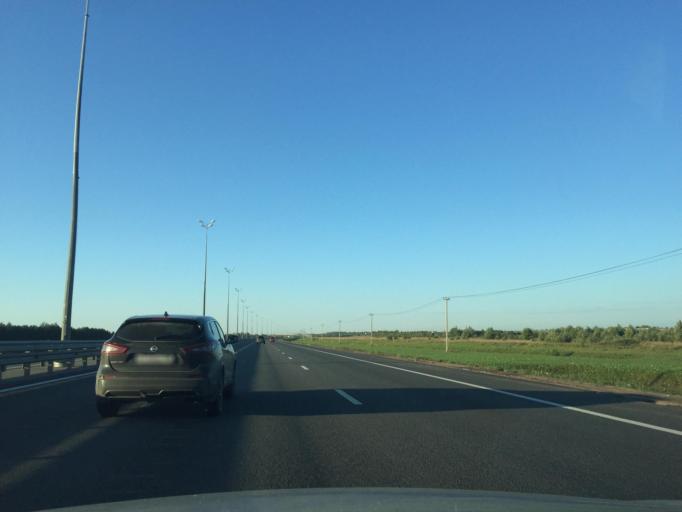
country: RU
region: Leningrad
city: Maloye Verevo
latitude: 59.6213
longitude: 30.1998
